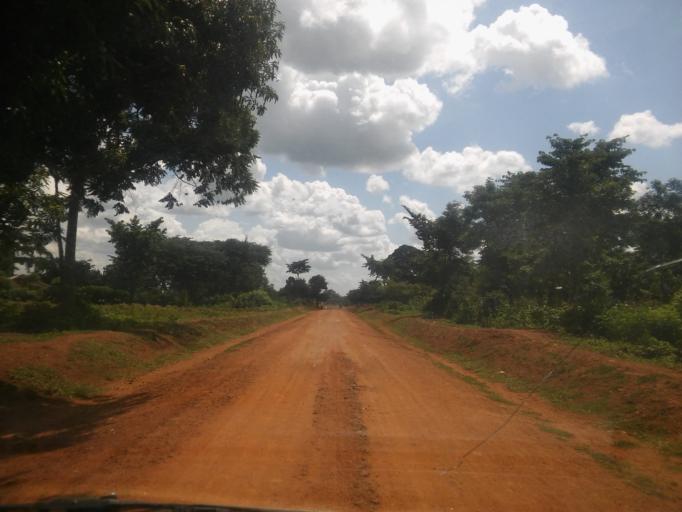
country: UG
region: Eastern Region
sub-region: Pallisa District
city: Pallisa
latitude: 1.1528
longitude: 33.8042
